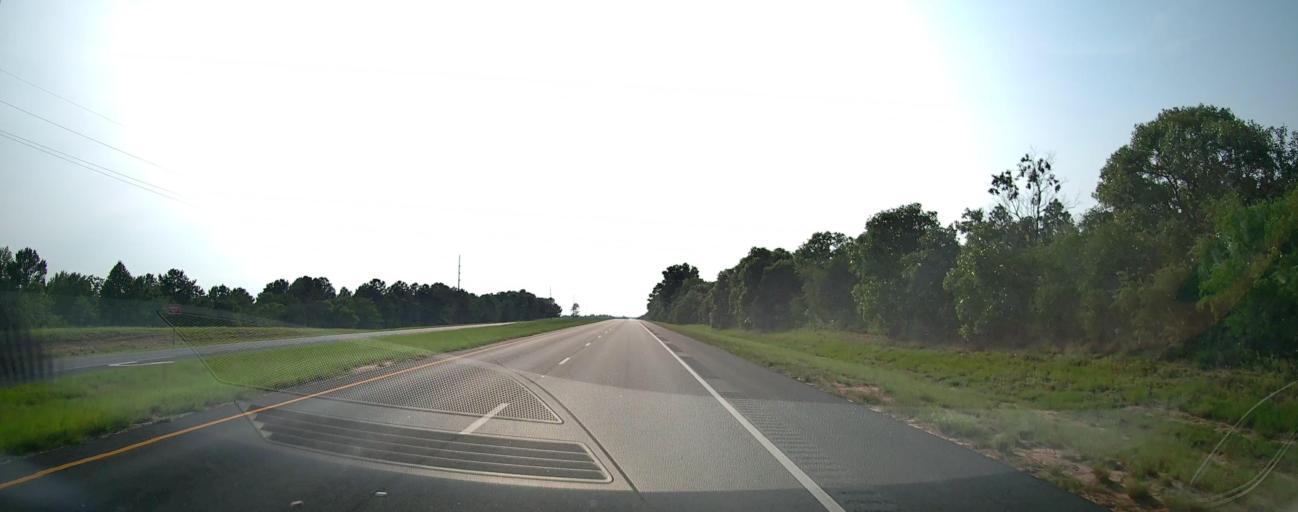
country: US
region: Georgia
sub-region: Taylor County
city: Butler
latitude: 32.5863
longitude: -84.3444
